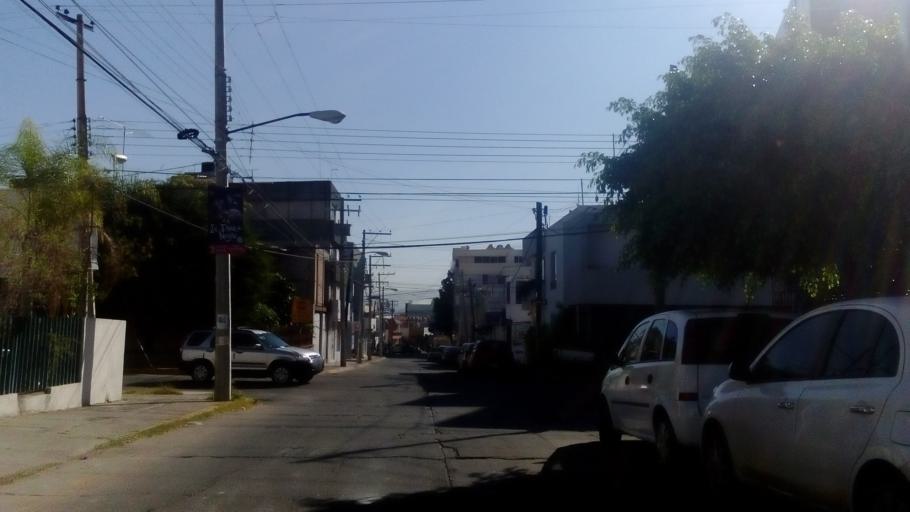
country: MX
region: Guanajuato
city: Leon
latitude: 21.1446
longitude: -101.6887
